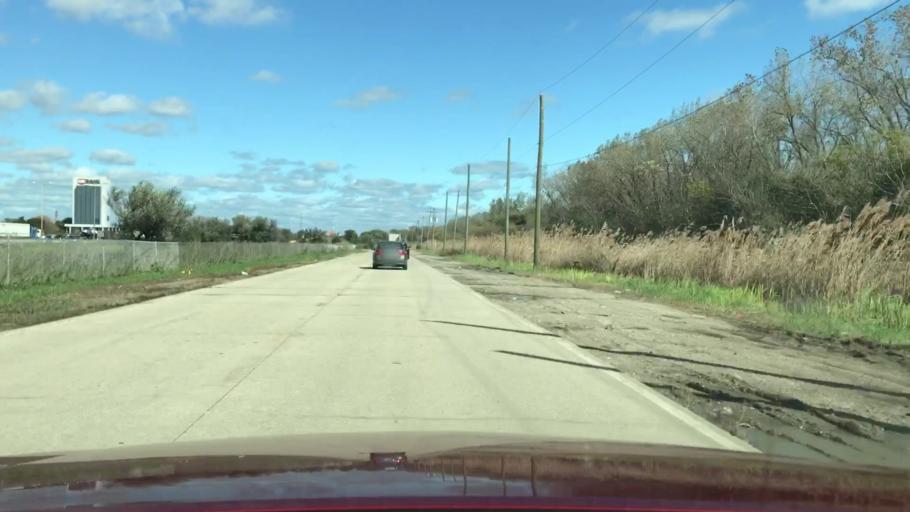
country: US
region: Illinois
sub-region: Cook County
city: Dolton
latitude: 41.6871
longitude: -87.5998
